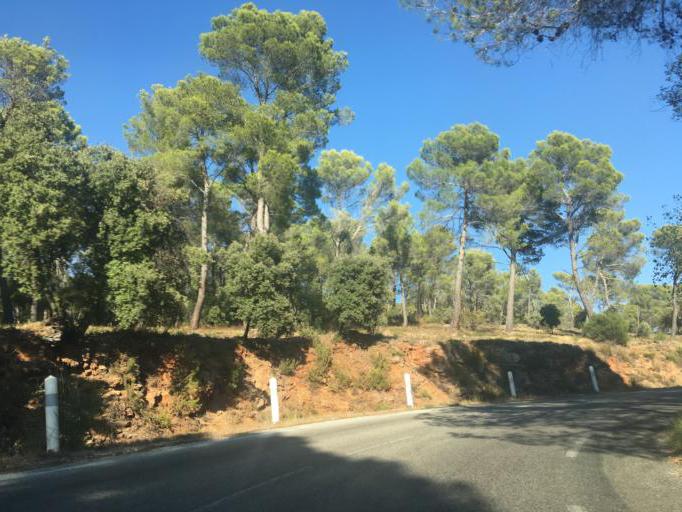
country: FR
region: Provence-Alpes-Cote d'Azur
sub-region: Departement du Var
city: Salernes
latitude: 43.5742
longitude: 6.2172
